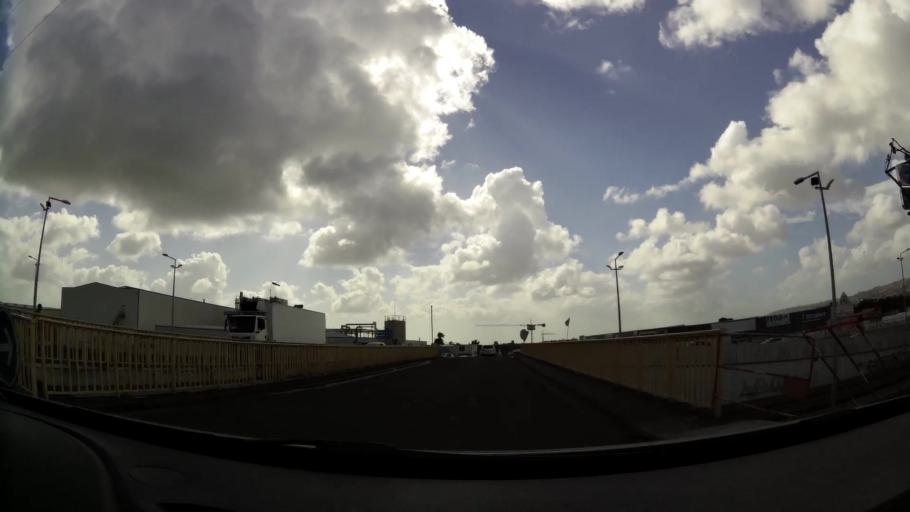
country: MQ
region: Martinique
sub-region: Martinique
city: Le Lamentin
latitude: 14.6094
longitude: -61.0054
